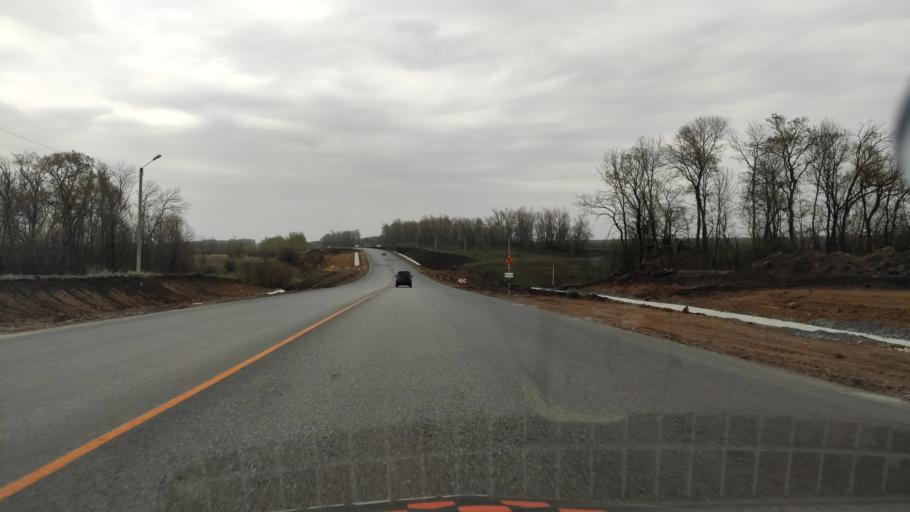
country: RU
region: Kursk
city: Gorshechnoye
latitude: 51.5496
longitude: 38.0479
